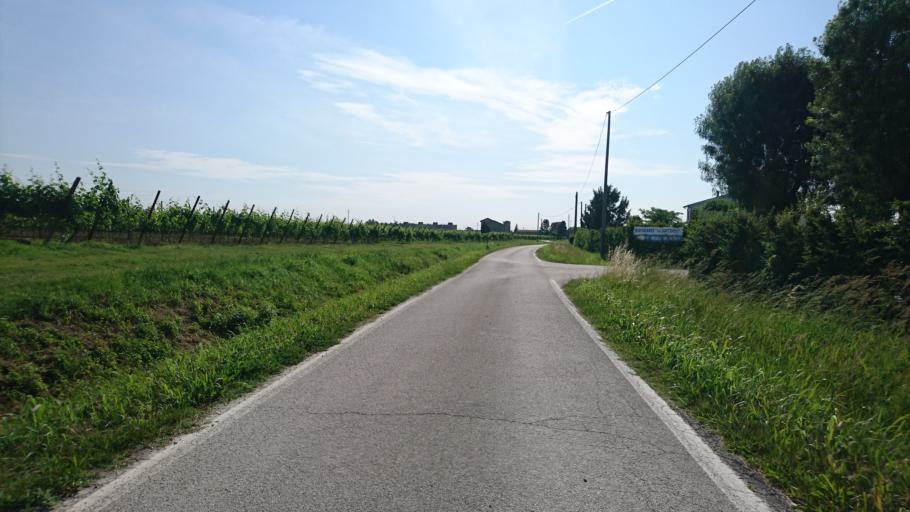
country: IT
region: Veneto
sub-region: Provincia di Padova
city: Merlara
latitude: 45.1747
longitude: 11.4360
